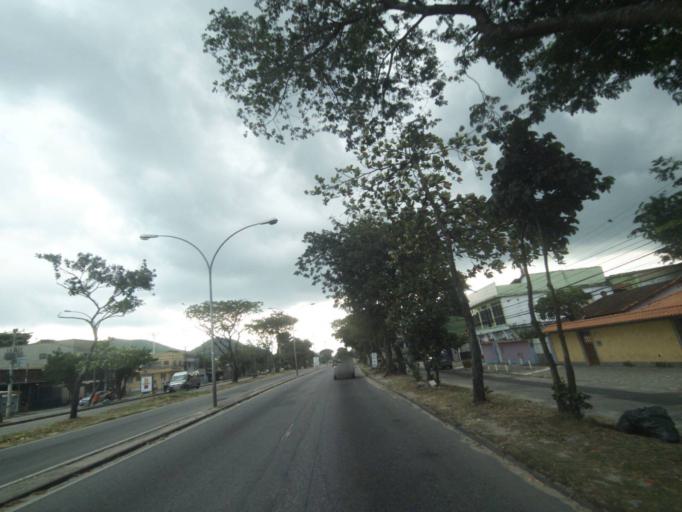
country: BR
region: Rio de Janeiro
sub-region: Nilopolis
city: Nilopolis
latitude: -22.8868
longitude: -43.3913
